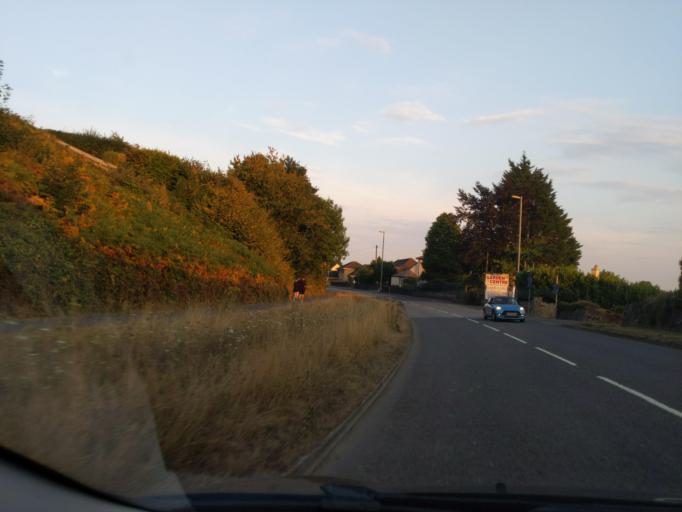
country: GB
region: England
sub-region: Cornwall
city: Liskeard
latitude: 50.4525
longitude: -4.4577
